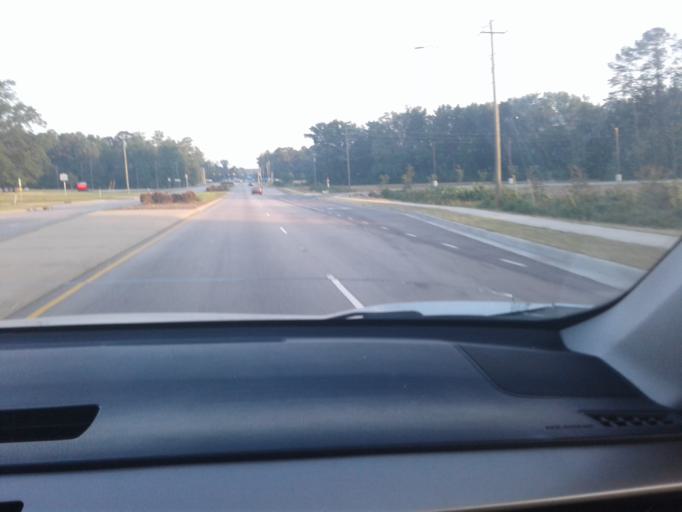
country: US
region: North Carolina
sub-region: Harnett County
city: Lillington
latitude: 35.4204
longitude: -78.8080
